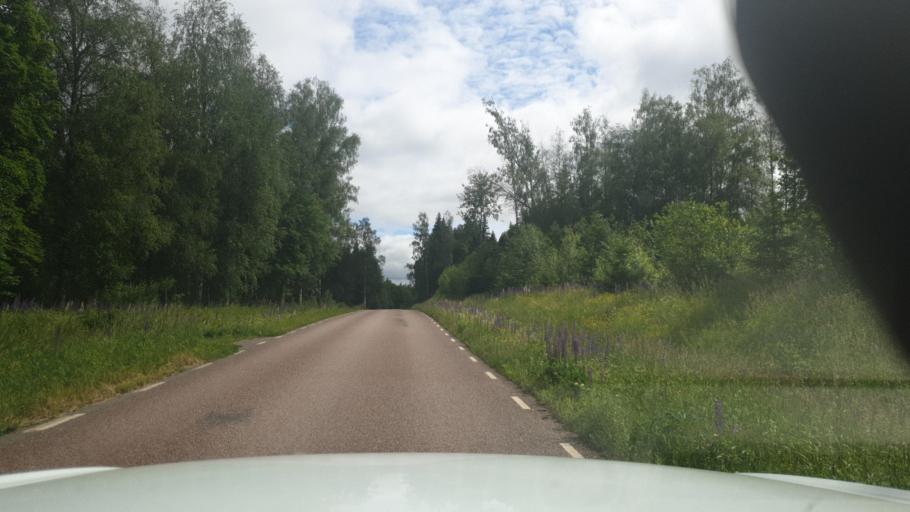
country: NO
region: Ostfold
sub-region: Romskog
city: Romskog
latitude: 59.7303
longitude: 12.0641
